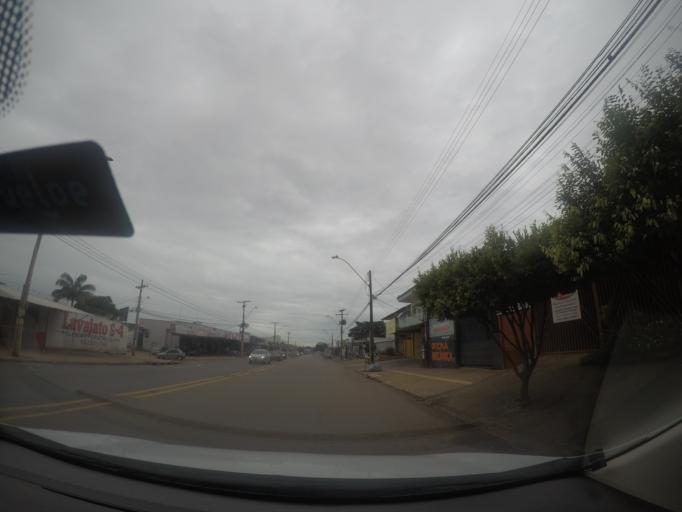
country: BR
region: Goias
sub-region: Goiania
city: Goiania
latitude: -16.6176
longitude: -49.2924
